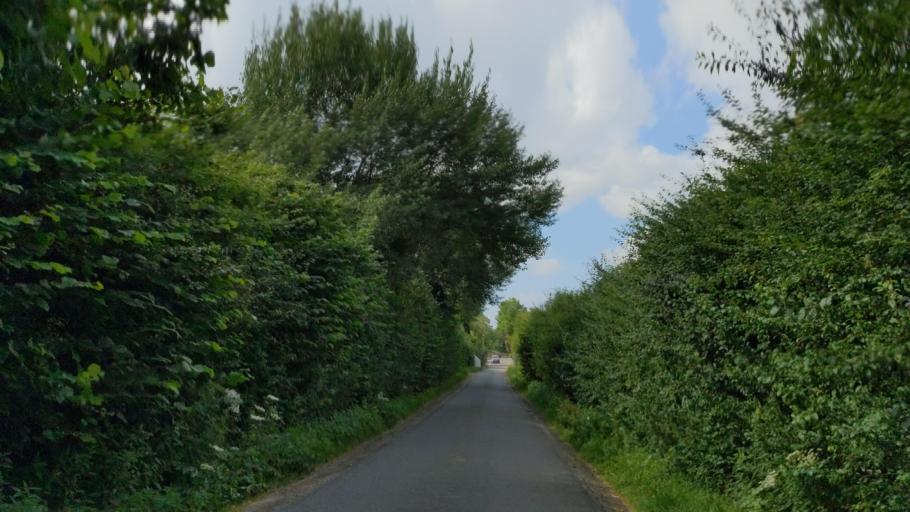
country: DE
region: Schleswig-Holstein
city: Badendorf
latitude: 53.8988
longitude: 10.5994
